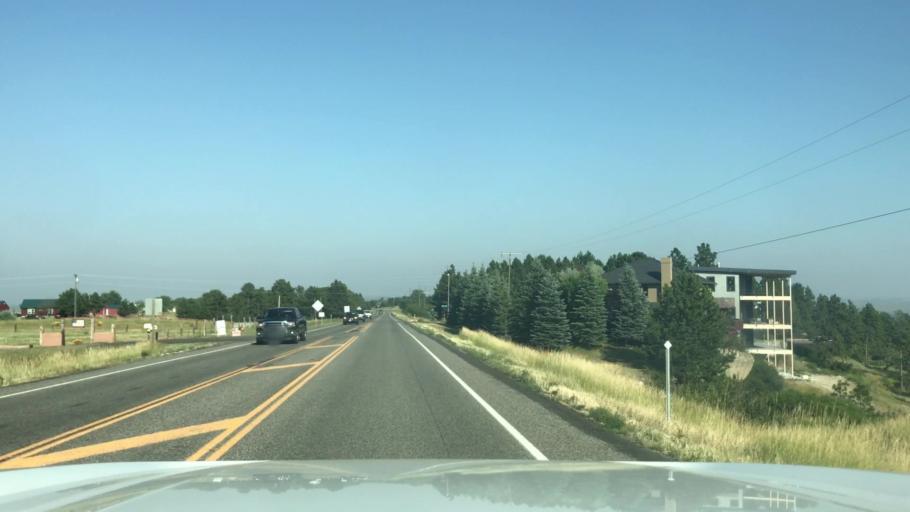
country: US
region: Montana
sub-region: Yellowstone County
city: Billings
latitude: 45.8052
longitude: -108.5888
